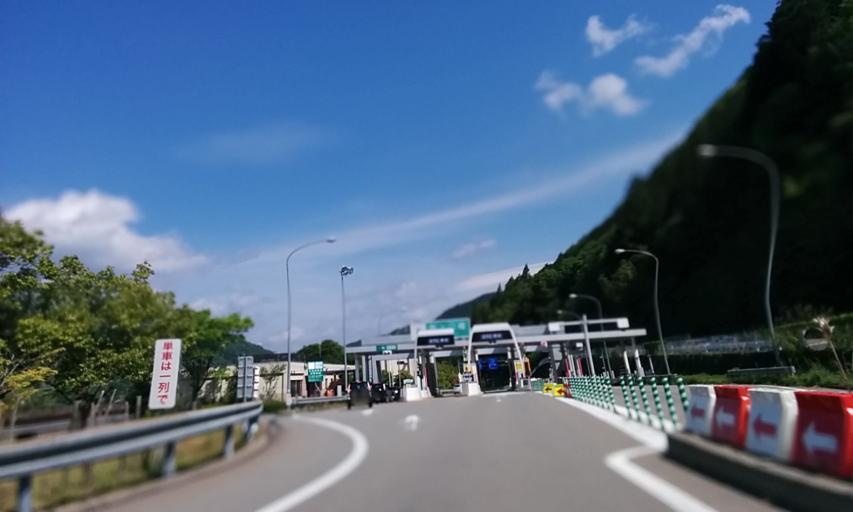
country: JP
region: Gifu
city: Gujo
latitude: 35.7501
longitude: 136.9479
